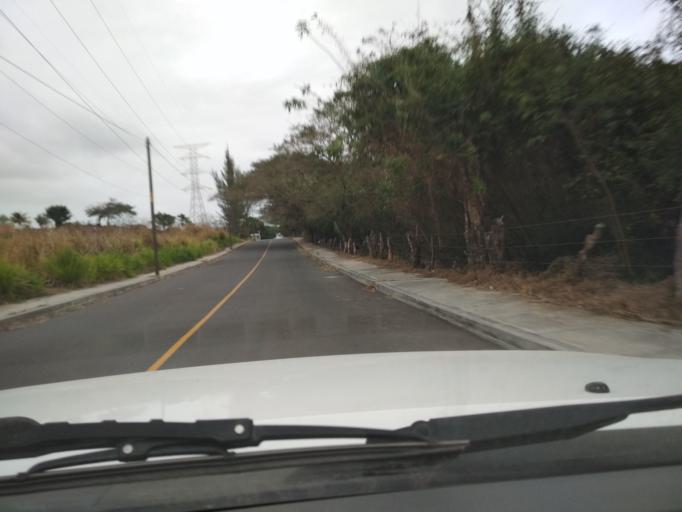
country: MX
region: Veracruz
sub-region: Medellin
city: Fraccionamiento Arboledas San Ramon
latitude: 19.0830
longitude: -96.1368
